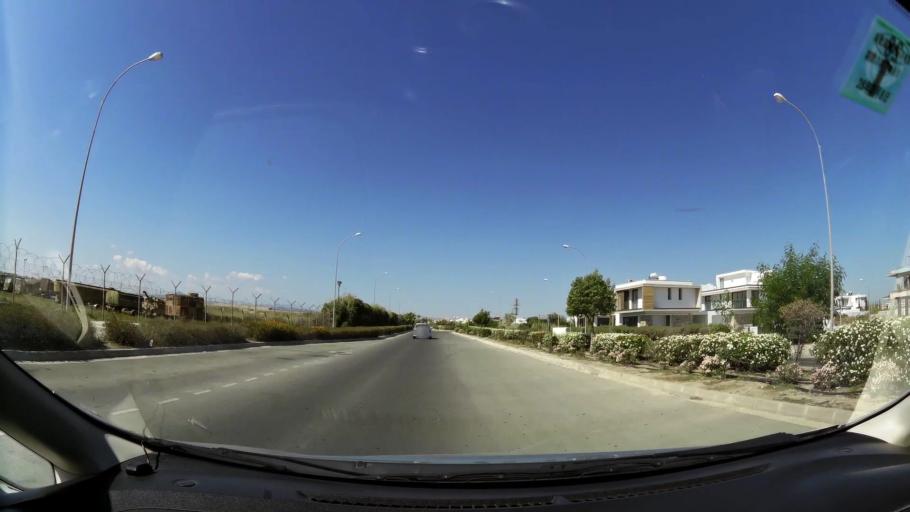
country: CY
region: Larnaka
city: Livadia
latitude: 34.9431
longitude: 33.6411
